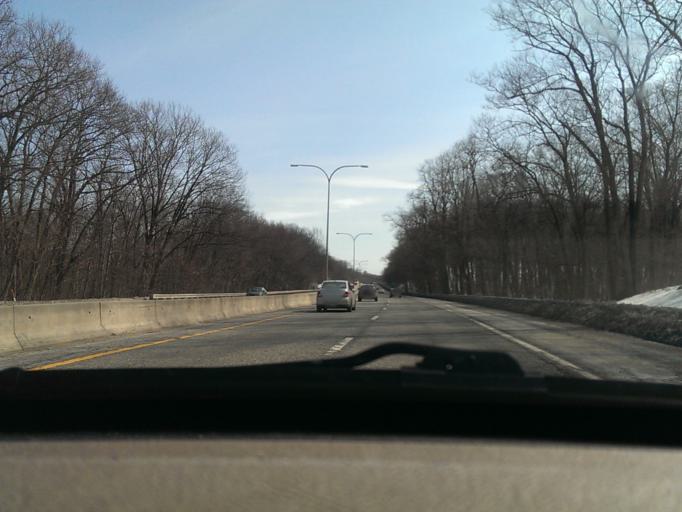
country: US
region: Rhode Island
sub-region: Providence County
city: Cumberland
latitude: 41.9111
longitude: -71.4516
